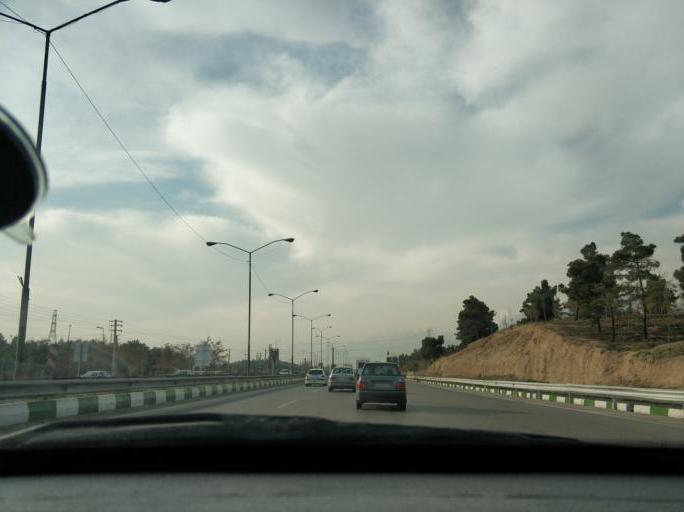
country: IR
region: Tehran
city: Tajrish
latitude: 35.7706
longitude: 51.5557
